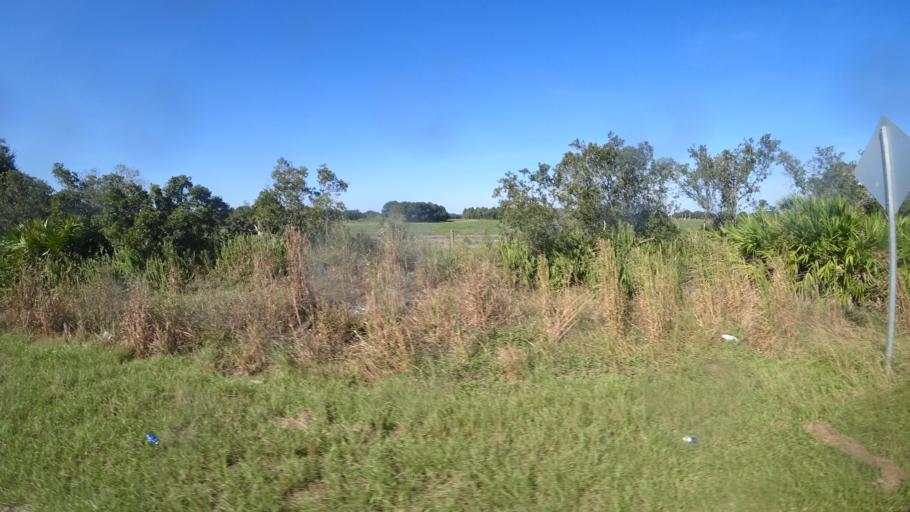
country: US
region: Florida
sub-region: Hillsborough County
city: Wimauma
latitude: 27.6015
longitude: -82.2928
